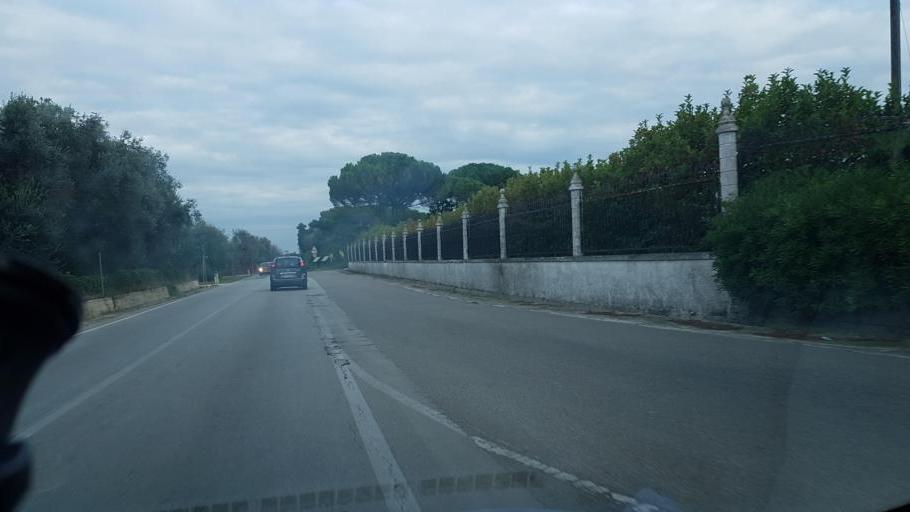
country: IT
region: Apulia
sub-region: Provincia di Brindisi
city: Francavilla Fontana
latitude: 40.5157
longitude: 17.6128
